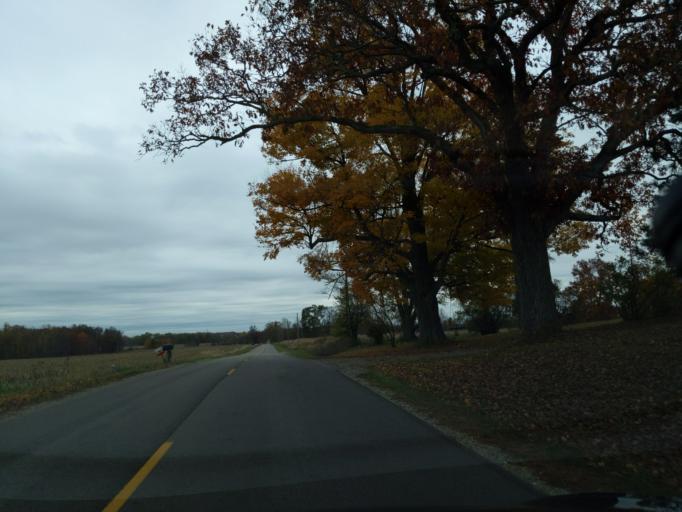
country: US
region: Michigan
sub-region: Eaton County
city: Eaton Rapids
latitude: 42.4272
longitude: -84.6103
